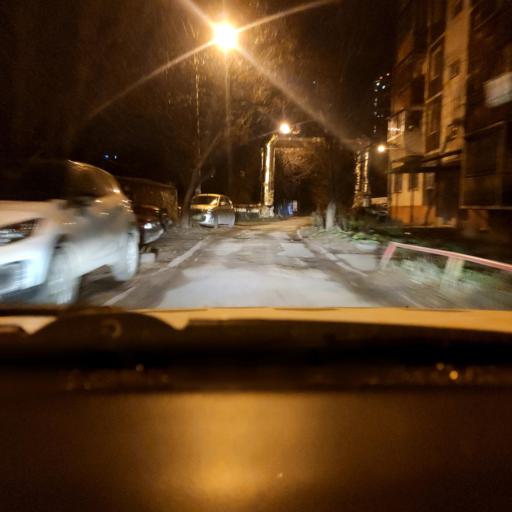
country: RU
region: Perm
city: Perm
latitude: 58.0004
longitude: 56.2148
